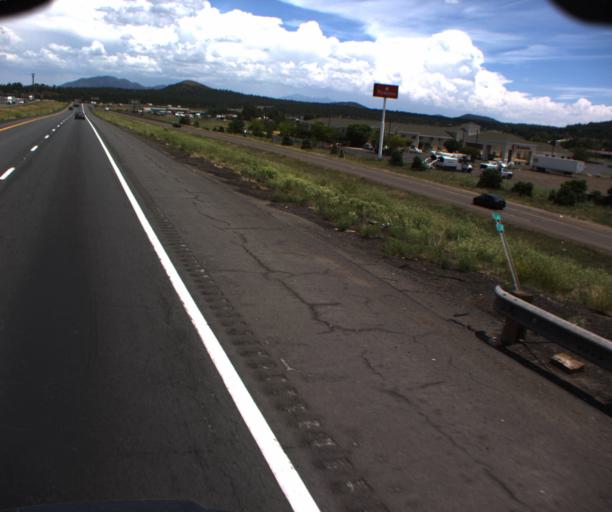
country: US
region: Arizona
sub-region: Coconino County
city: Williams
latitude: 35.2591
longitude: -112.1924
